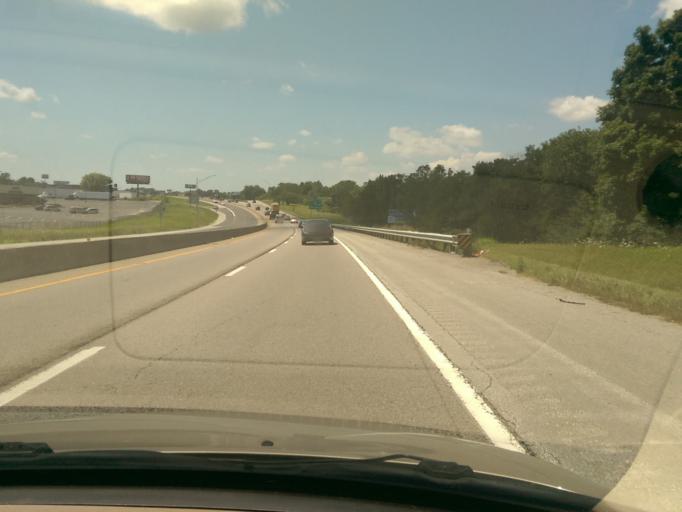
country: US
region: Missouri
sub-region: Boone County
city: Columbia
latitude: 38.9693
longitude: -92.3439
